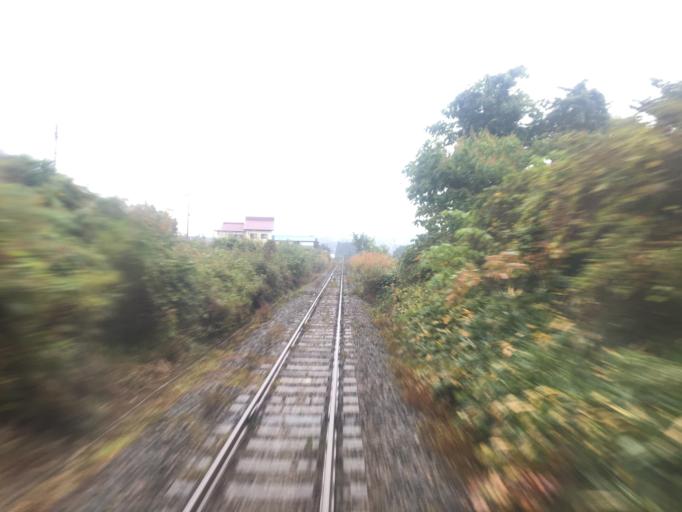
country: JP
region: Yamagata
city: Shinjo
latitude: 38.7095
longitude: 140.3144
